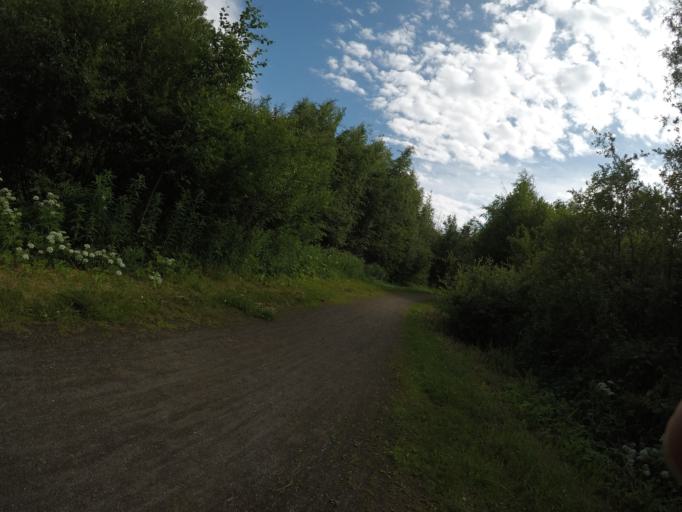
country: FI
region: Haeme
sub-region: Haemeenlinna
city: Haemeenlinna
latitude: 60.9831
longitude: 24.3923
